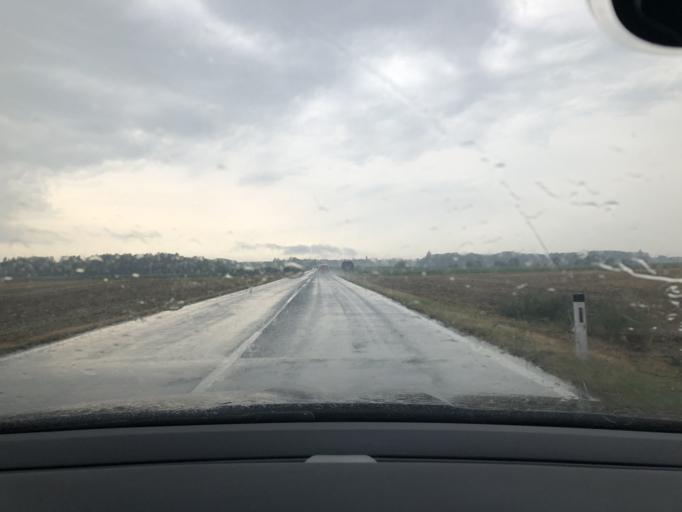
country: AT
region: Lower Austria
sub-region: Politischer Bezirk Ganserndorf
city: Marchegg
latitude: 48.3091
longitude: 16.8583
